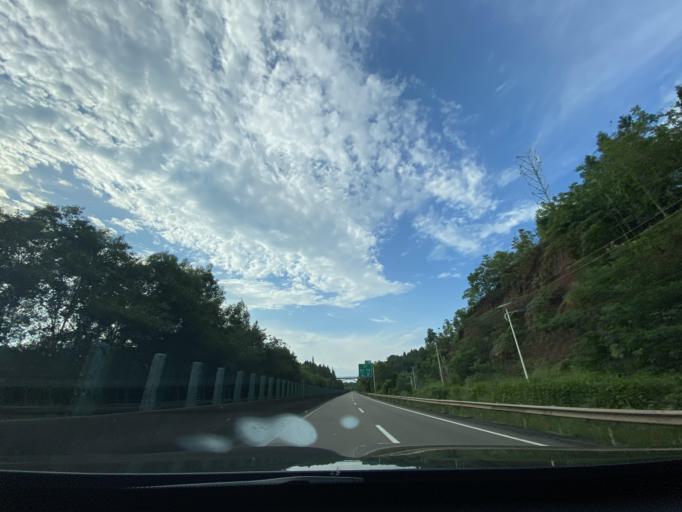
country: CN
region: Sichuan
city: Jiancheng
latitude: 30.2646
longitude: 104.6057
